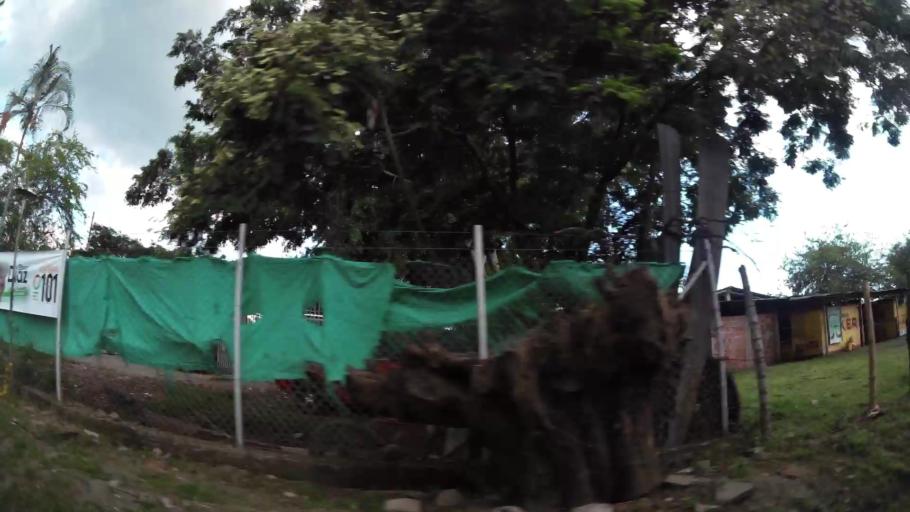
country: CO
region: Valle del Cauca
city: Cali
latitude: 3.4040
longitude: -76.4981
